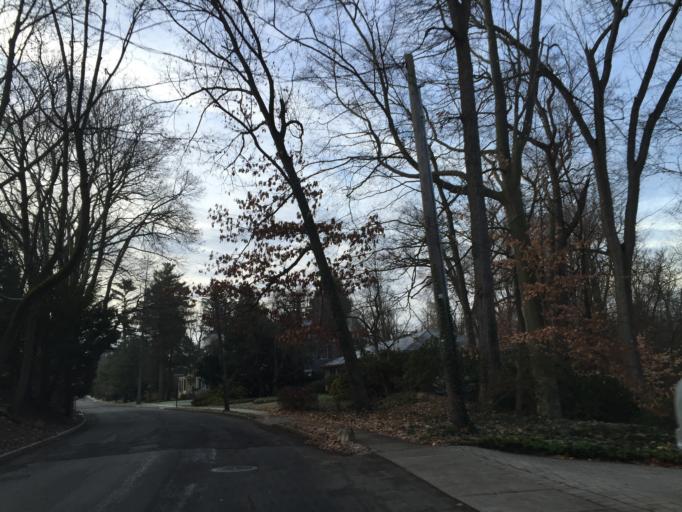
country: US
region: New Jersey
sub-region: Morris County
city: Chatham
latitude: 40.7128
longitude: -74.3725
